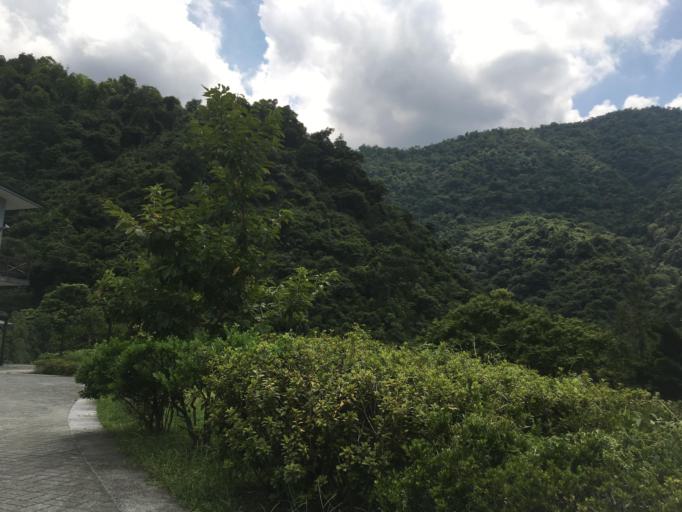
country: TW
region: Taiwan
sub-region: Yilan
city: Yilan
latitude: 24.6064
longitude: 121.7476
